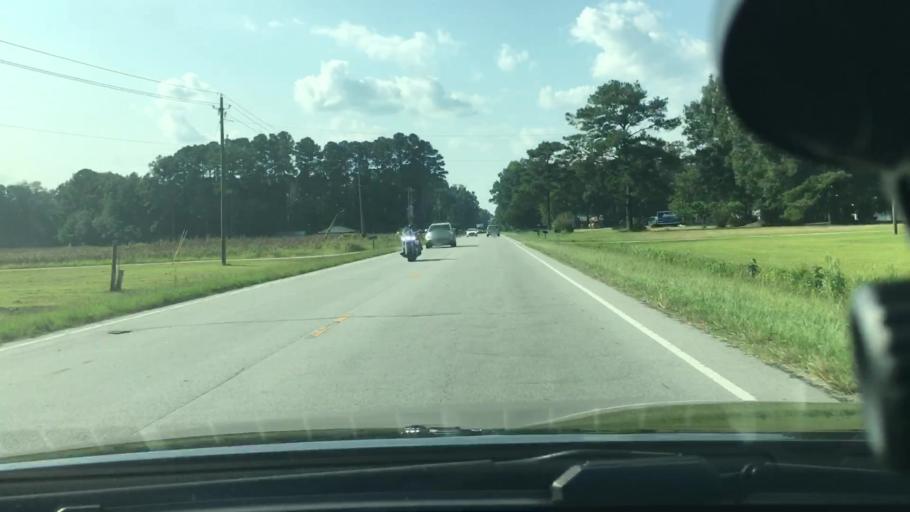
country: US
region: North Carolina
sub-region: Craven County
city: Vanceboro
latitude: 35.2566
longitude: -77.0964
